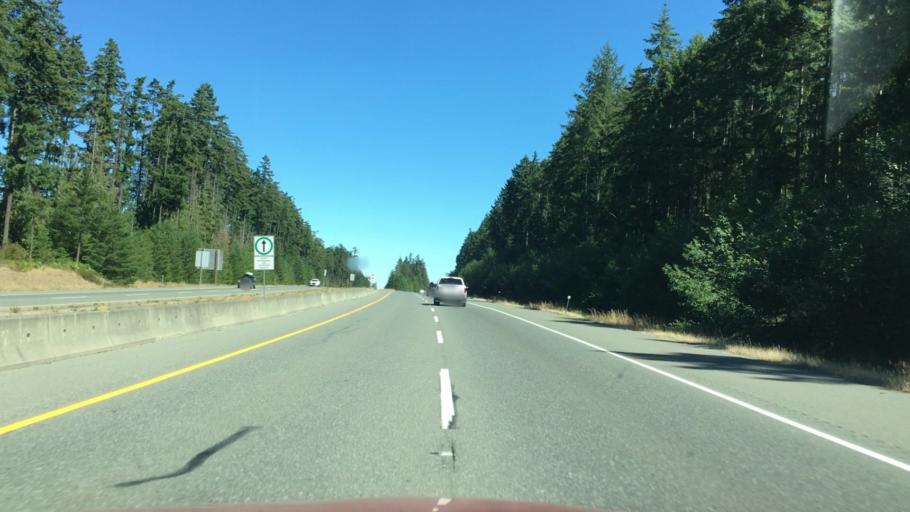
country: CA
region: British Columbia
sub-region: Regional District of Nanaimo
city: Parksville
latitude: 49.3188
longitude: -124.4003
